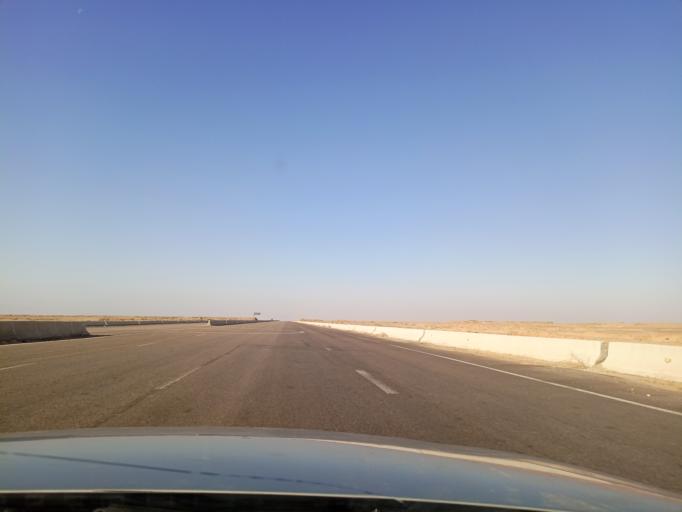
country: EG
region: Muhafazat al Fayyum
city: Tamiyah
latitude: 29.6209
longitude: 30.9469
